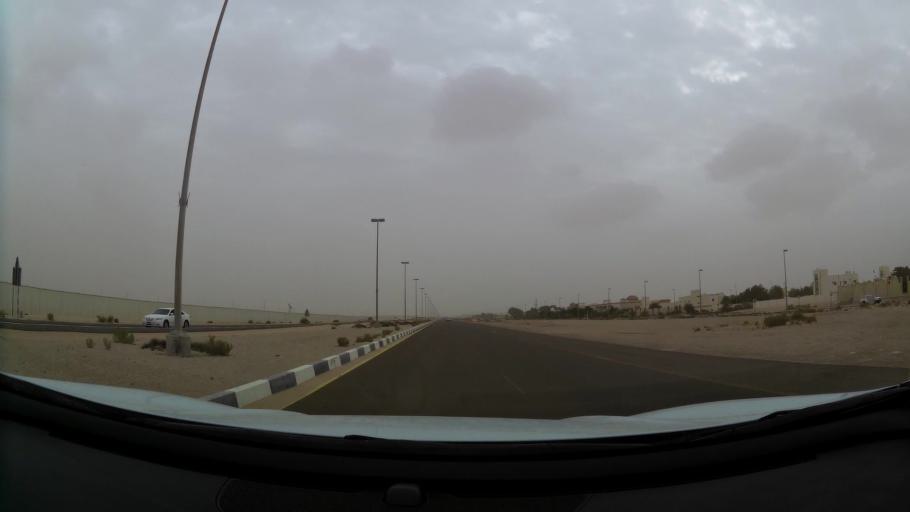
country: AE
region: Abu Dhabi
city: Abu Dhabi
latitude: 24.4259
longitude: 54.7145
